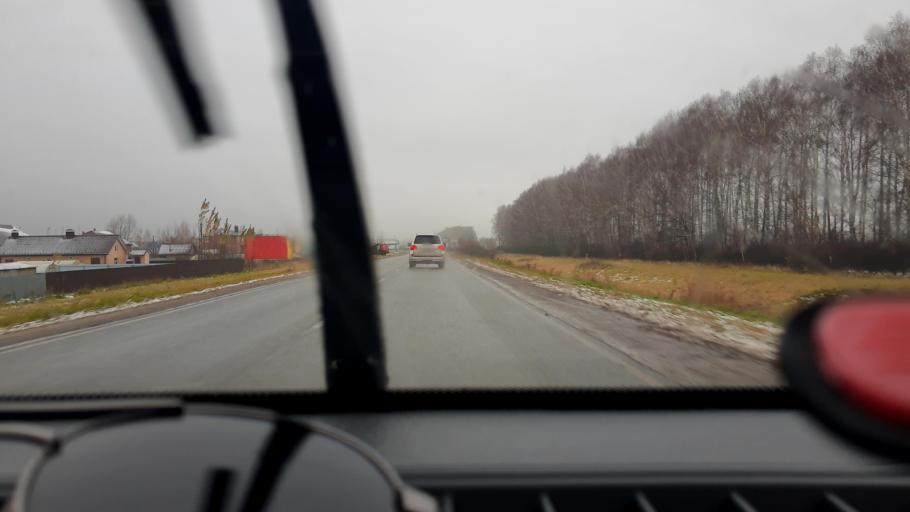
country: RU
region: Bashkortostan
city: Kabakovo
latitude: 54.6042
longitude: 56.1929
